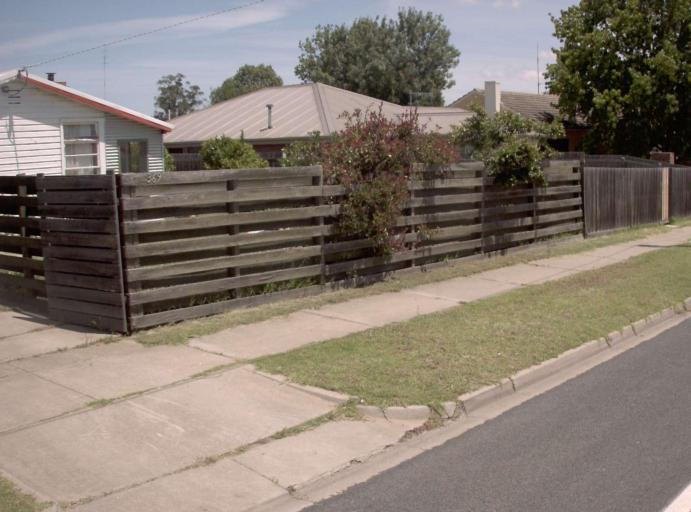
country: AU
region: Victoria
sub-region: East Gippsland
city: Bairnsdale
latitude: -37.8298
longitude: 147.6147
